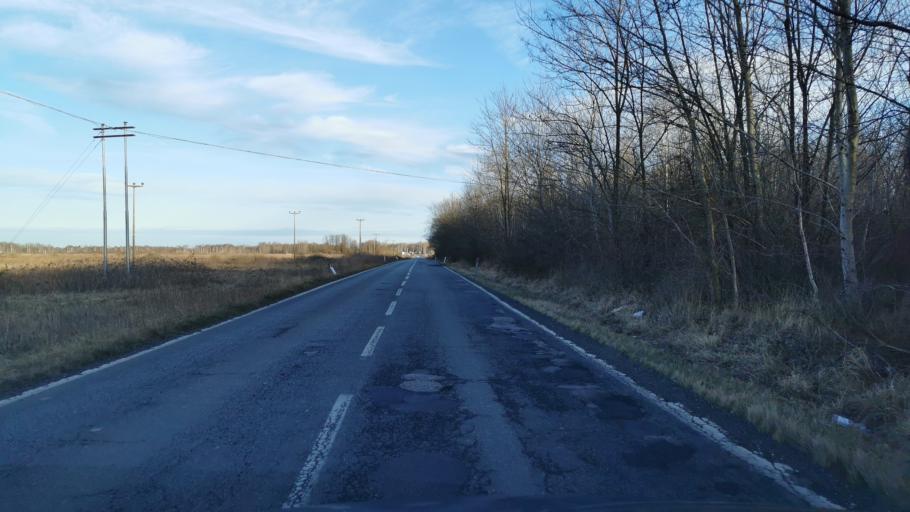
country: IT
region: Piedmont
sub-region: Provincia di Torino
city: San Francesco al Campo
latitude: 45.2486
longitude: 7.6484
